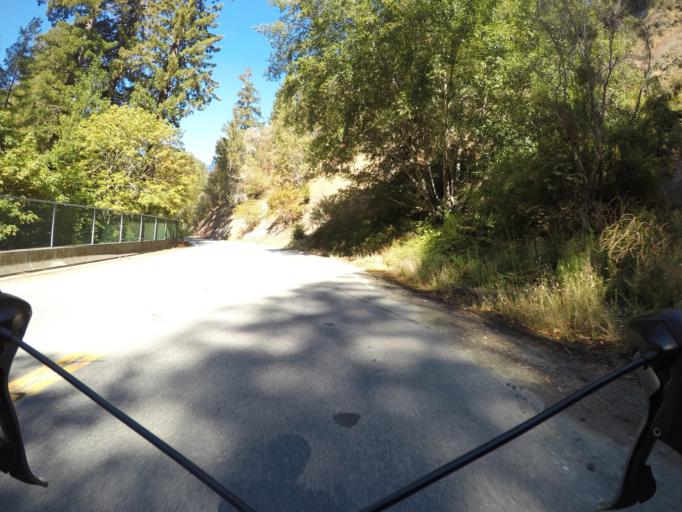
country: US
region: California
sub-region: San Mateo County
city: Portola Valley
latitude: 37.3302
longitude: -122.2694
